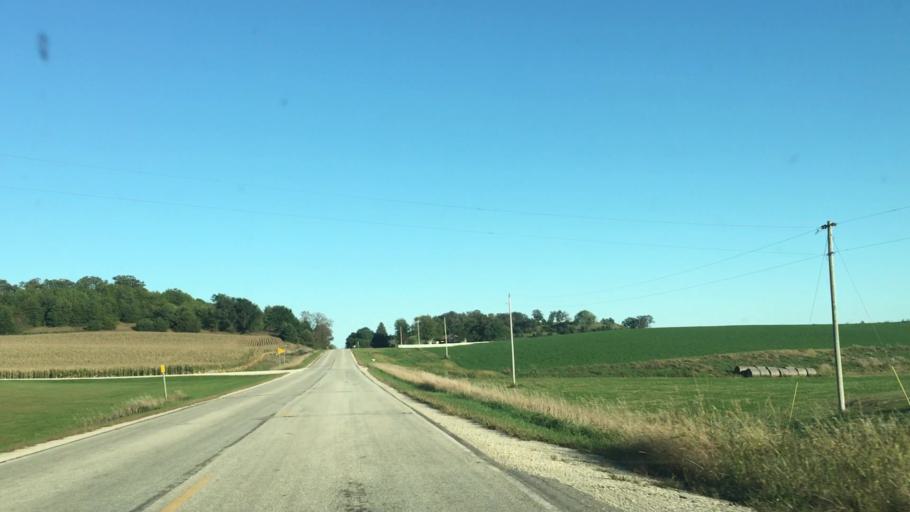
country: US
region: Minnesota
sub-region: Fillmore County
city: Chatfield
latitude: 43.8426
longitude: -92.0906
